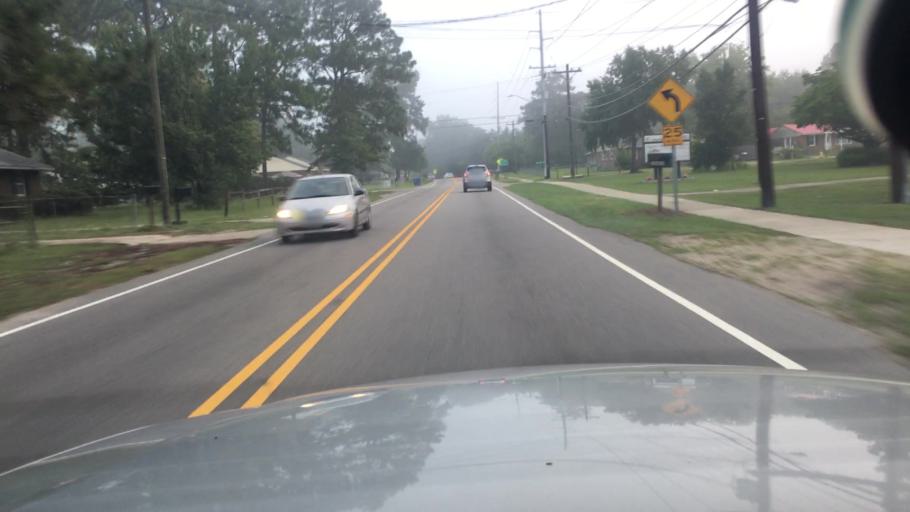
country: US
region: North Carolina
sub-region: Cumberland County
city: Hope Mills
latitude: 35.0198
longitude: -78.9401
